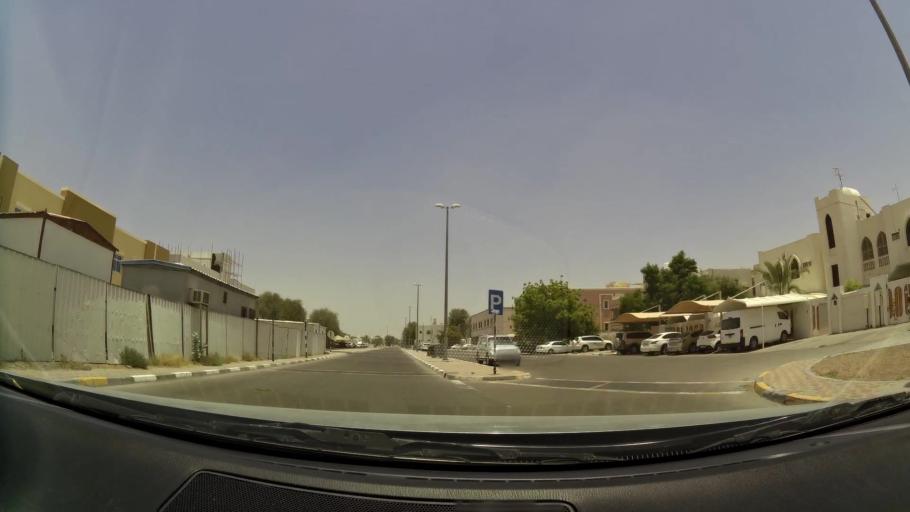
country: OM
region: Al Buraimi
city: Al Buraymi
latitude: 24.2611
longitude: 55.7275
